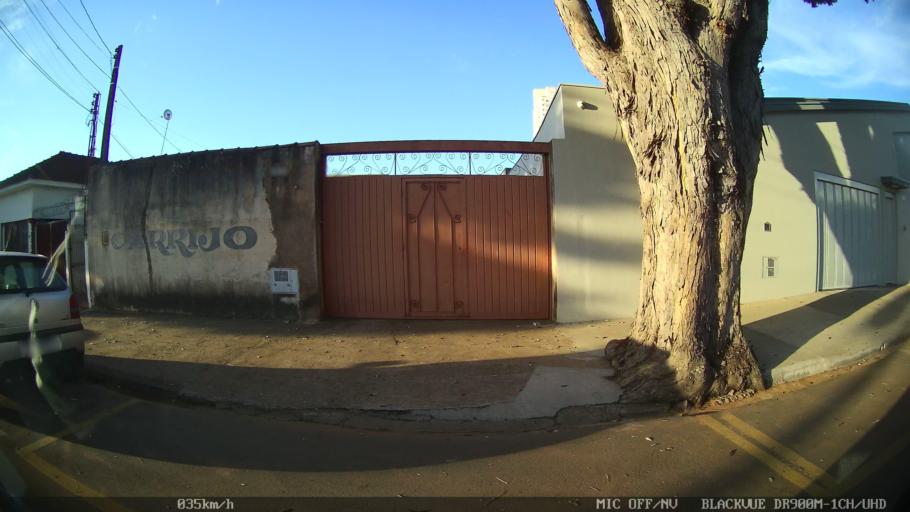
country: BR
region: Sao Paulo
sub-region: Franca
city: Franca
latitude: -20.5270
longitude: -47.3920
